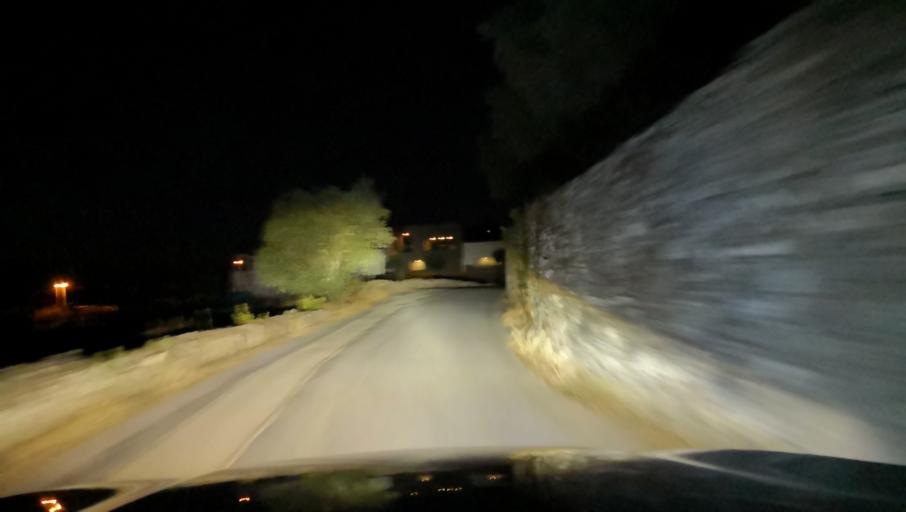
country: PT
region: Vila Real
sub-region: Peso da Regua
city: Peso da Regua
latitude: 41.1734
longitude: -7.7290
